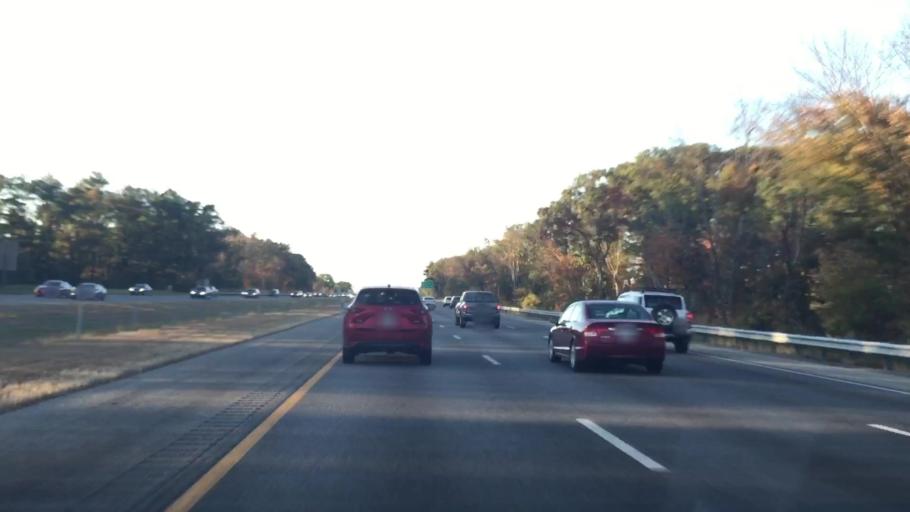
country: US
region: Massachusetts
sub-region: Middlesex County
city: Billerica
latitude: 42.5299
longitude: -71.2735
